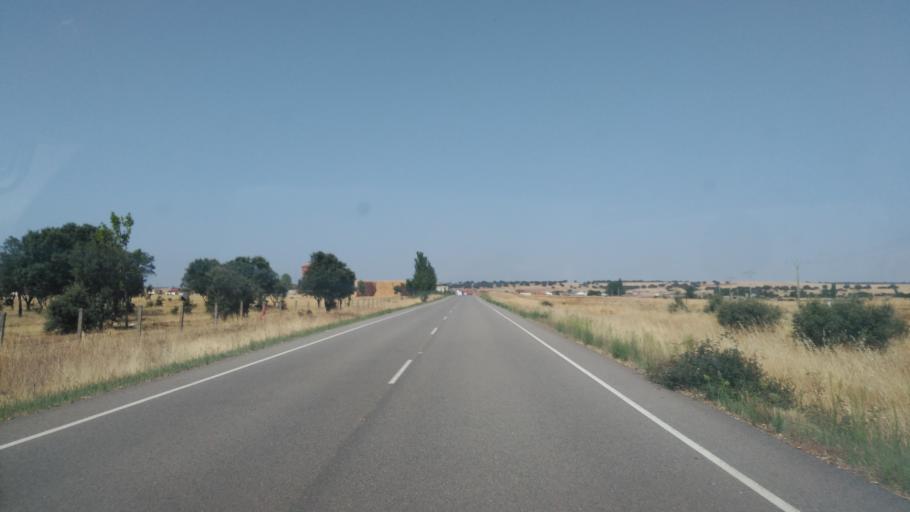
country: ES
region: Castille and Leon
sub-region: Provincia de Salamanca
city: Cabrillas
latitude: 40.7343
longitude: -6.1693
